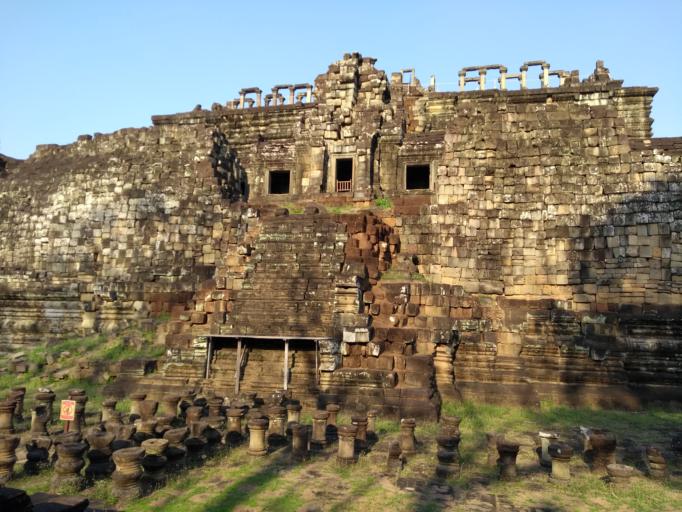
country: KH
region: Siem Reap
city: Siem Reap
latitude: 13.4437
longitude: 103.8556
